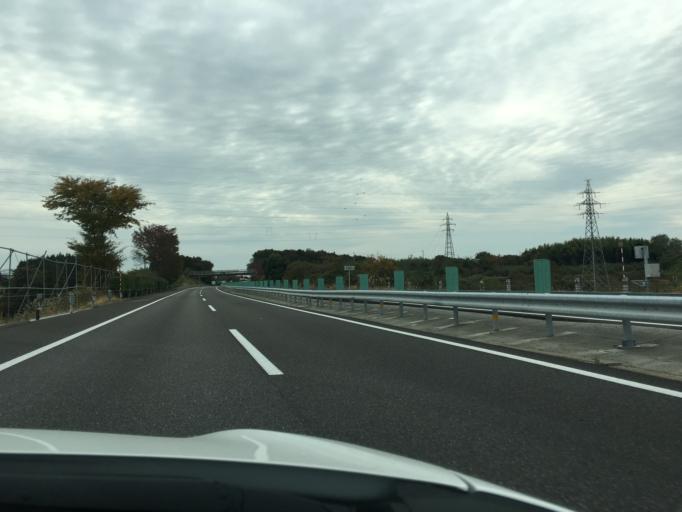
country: JP
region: Fukushima
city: Sukagawa
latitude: 37.2754
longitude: 140.3506
